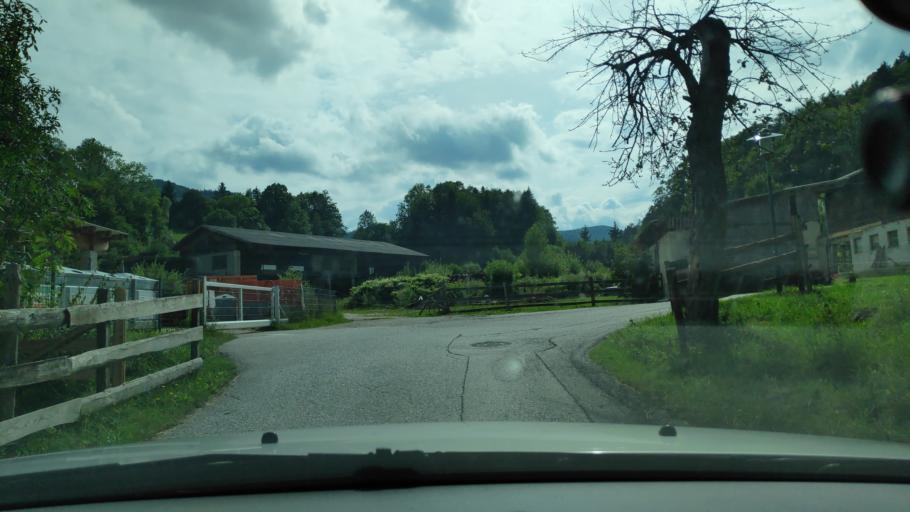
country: AT
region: Lower Austria
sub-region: Politischer Bezirk Wiener Neustadt
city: Miesenbach
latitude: 47.8320
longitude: 15.9761
